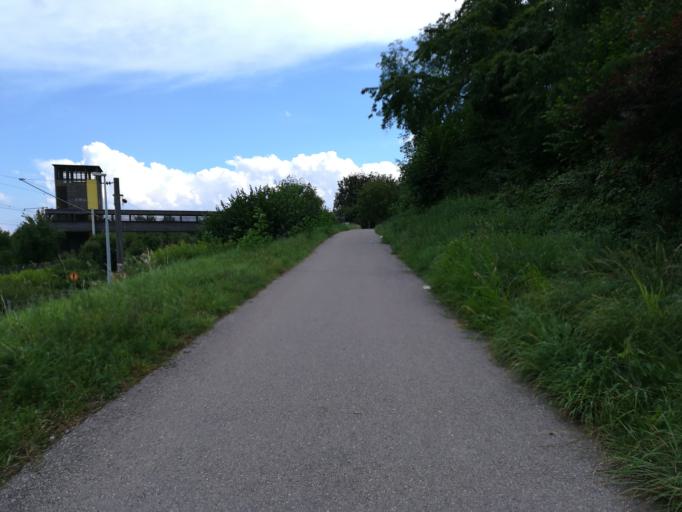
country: DE
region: Baden-Wuerttemberg
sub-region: Freiburg Region
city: Singen
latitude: 47.7595
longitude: 8.8271
